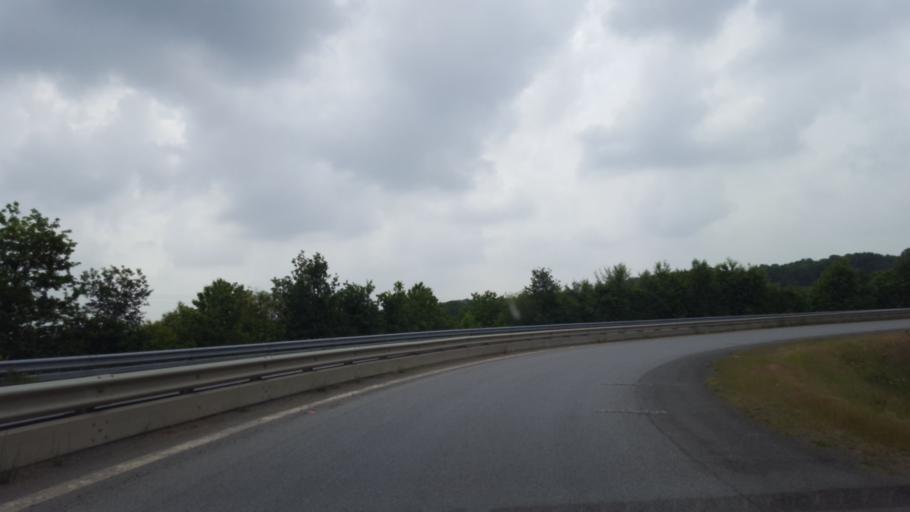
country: FR
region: Brittany
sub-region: Departement d'Ille-et-Vilaine
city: Grand-Fougeray
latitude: 47.7461
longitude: -1.7137
